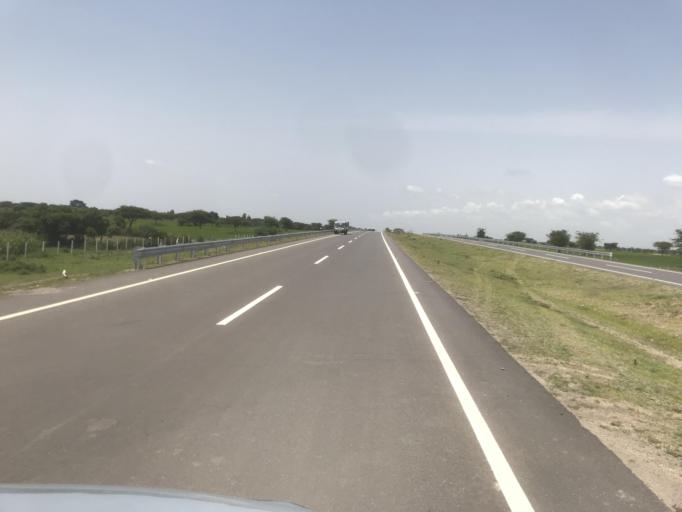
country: ET
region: Oromiya
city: Mojo
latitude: 8.2692
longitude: 38.9068
